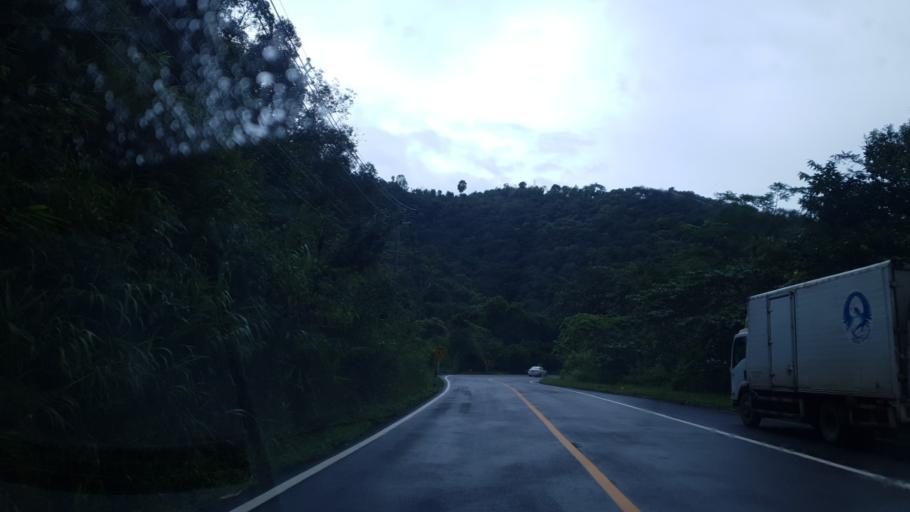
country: TH
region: Mae Hong Son
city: Ban Huai I Huak
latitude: 18.1419
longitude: 98.1083
